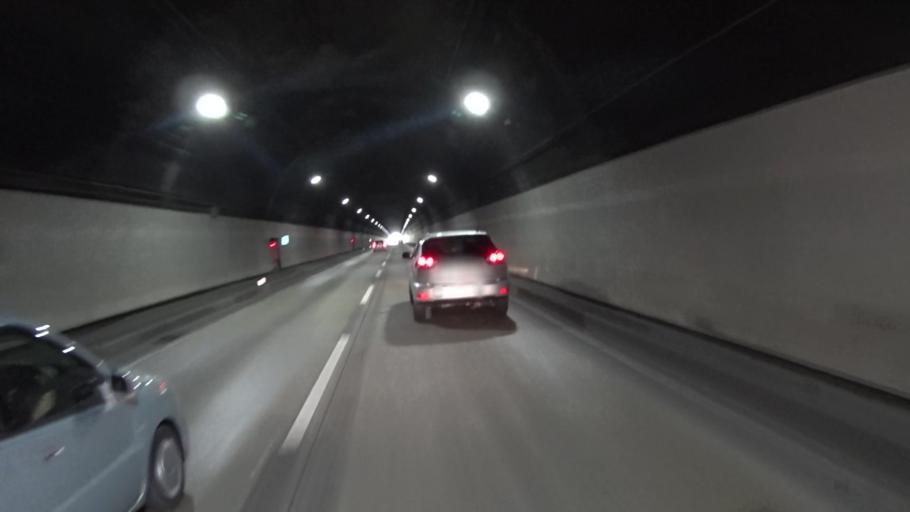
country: JP
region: Shiga Prefecture
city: Otsu-shi
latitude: 35.0120
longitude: 135.8420
